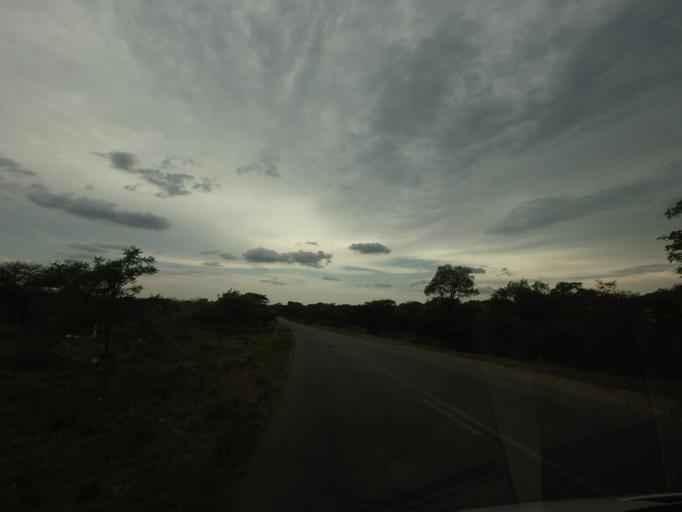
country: ZA
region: Limpopo
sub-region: Mopani District Municipality
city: Hoedspruit
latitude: -24.5077
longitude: 30.9109
